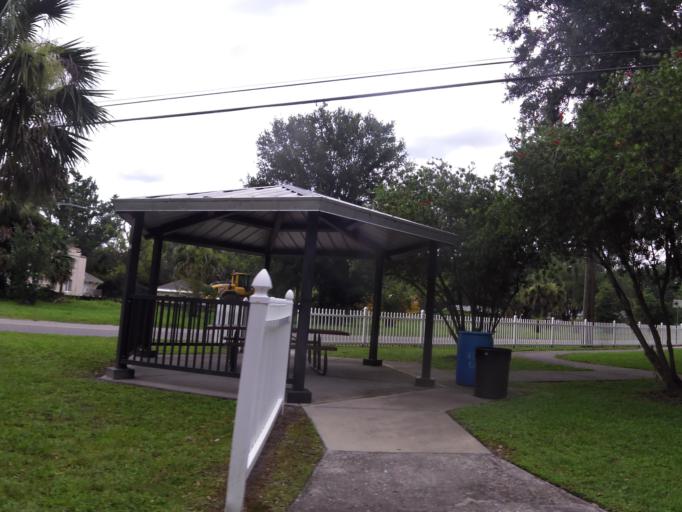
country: US
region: Florida
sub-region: Putnam County
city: East Palatka
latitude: 29.7192
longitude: -81.5075
